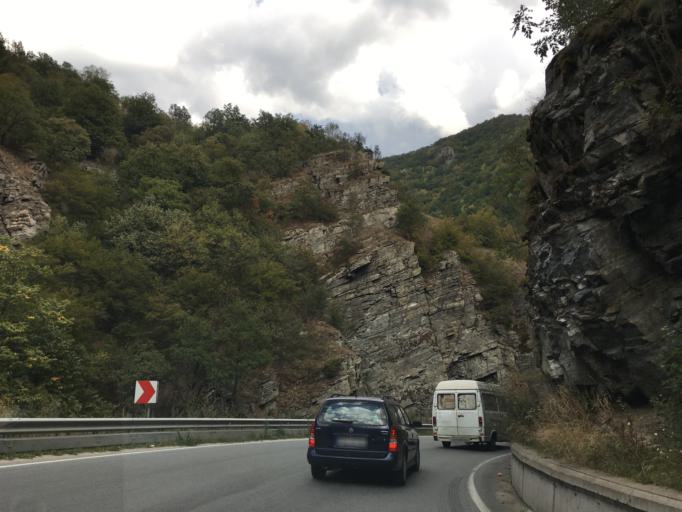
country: BG
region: Pazardzhik
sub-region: Obshtina Septemvri
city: Septemvri
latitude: 42.1032
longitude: 24.0979
